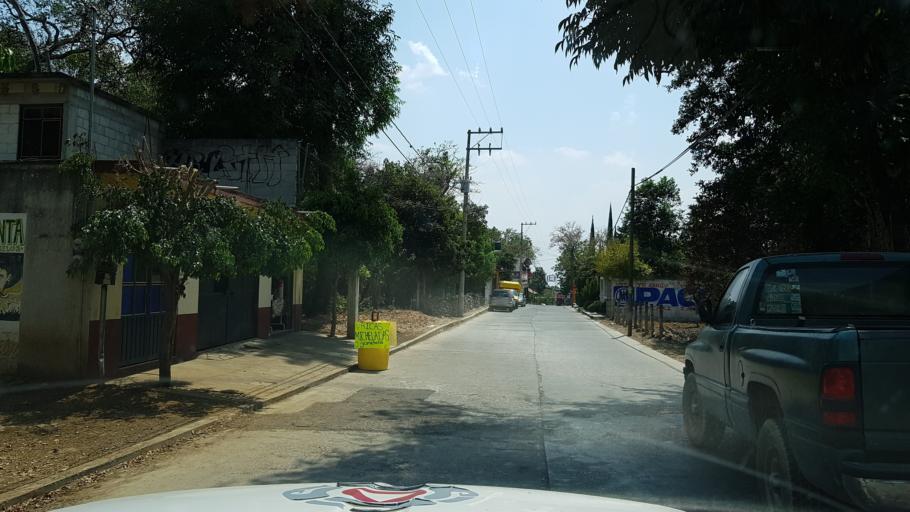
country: MX
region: Morelos
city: Ocuituco
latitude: 18.8846
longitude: -98.8147
